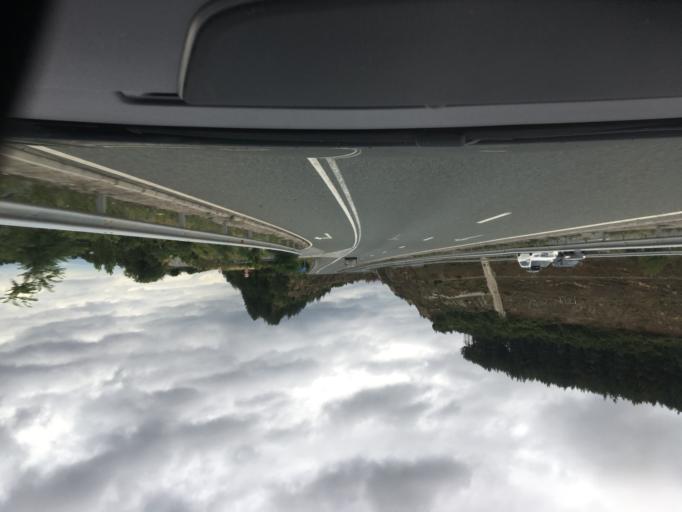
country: BG
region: Pernik
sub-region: Obshtina Pernik
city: Pernik
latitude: 42.4836
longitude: 23.1196
